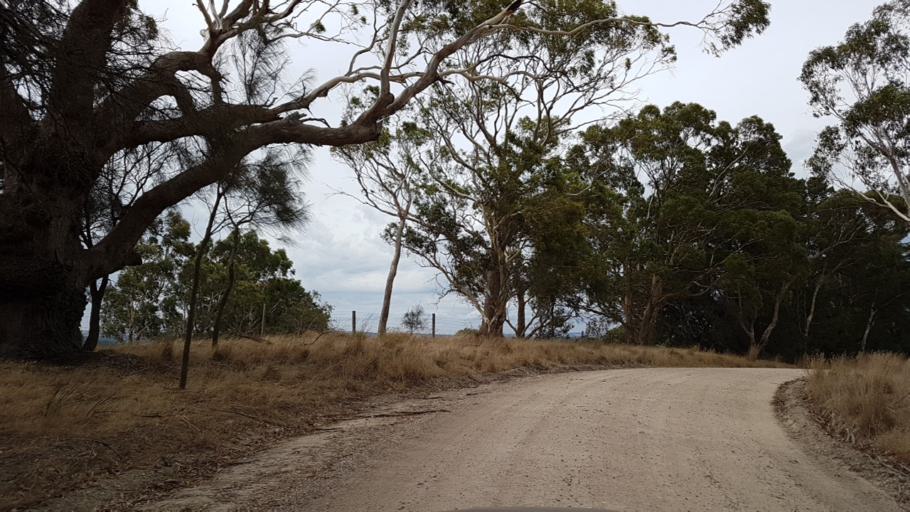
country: AU
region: South Australia
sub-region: Adelaide Hills
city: Birdwood
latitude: -34.7622
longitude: 138.9928
